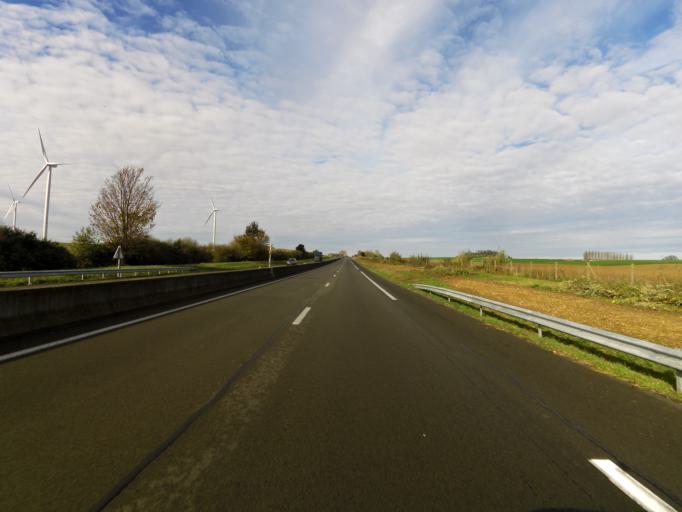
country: FR
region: Picardie
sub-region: Departement de l'Aisne
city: Charmes
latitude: 49.7047
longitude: 3.4342
